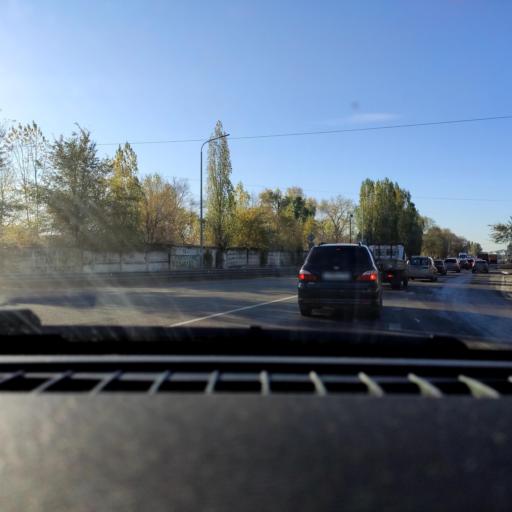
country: RU
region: Voronezj
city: Novaya Usman'
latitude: 51.6460
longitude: 39.2976
